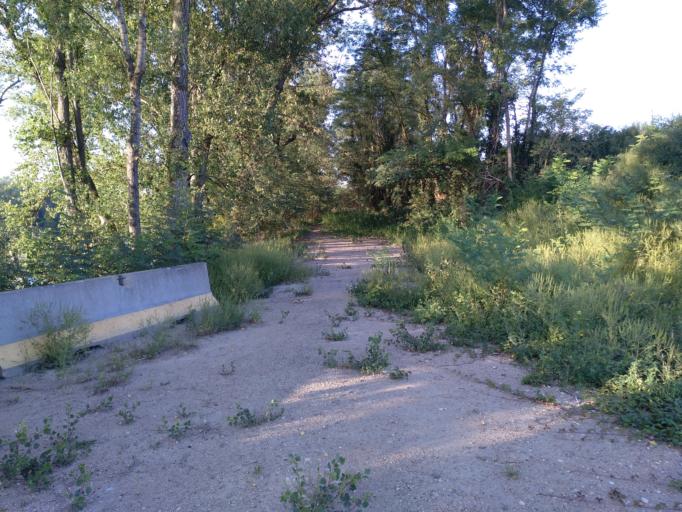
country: FR
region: Rhone-Alpes
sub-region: Departement de l'Isere
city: Chasse-sur-Rhone
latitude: 45.5954
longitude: 4.7902
